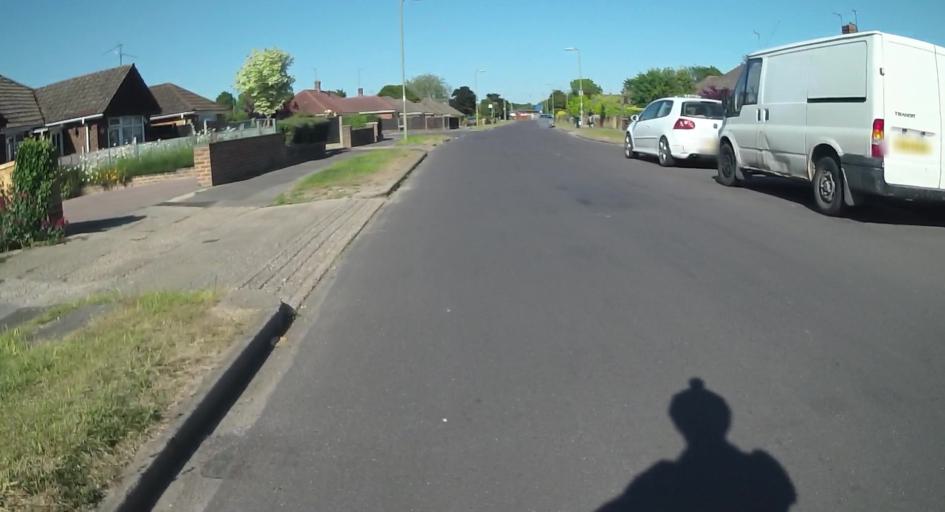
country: GB
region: England
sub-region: Hampshire
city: Basingstoke
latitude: 51.2508
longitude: -1.1160
